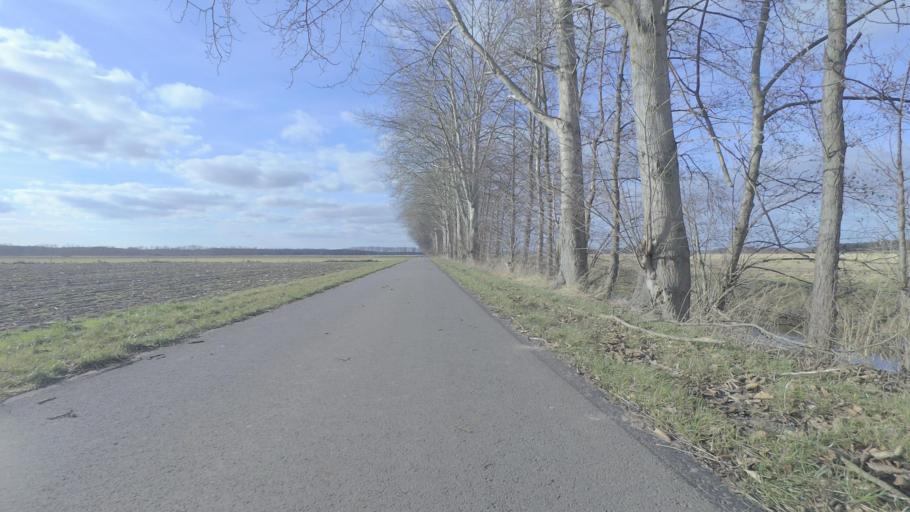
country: DE
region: Brandenburg
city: Trebbin
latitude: 52.2201
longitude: 13.2816
